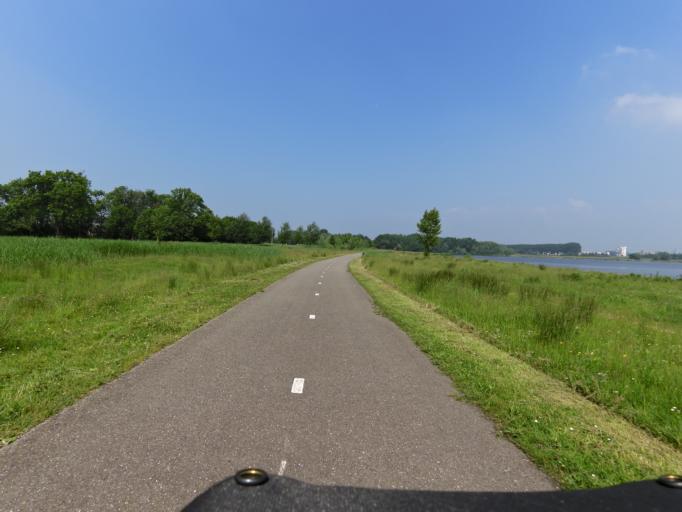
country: NL
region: South Holland
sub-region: Gemeente Maassluis
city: Maassluis
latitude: 51.8742
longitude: 4.2225
